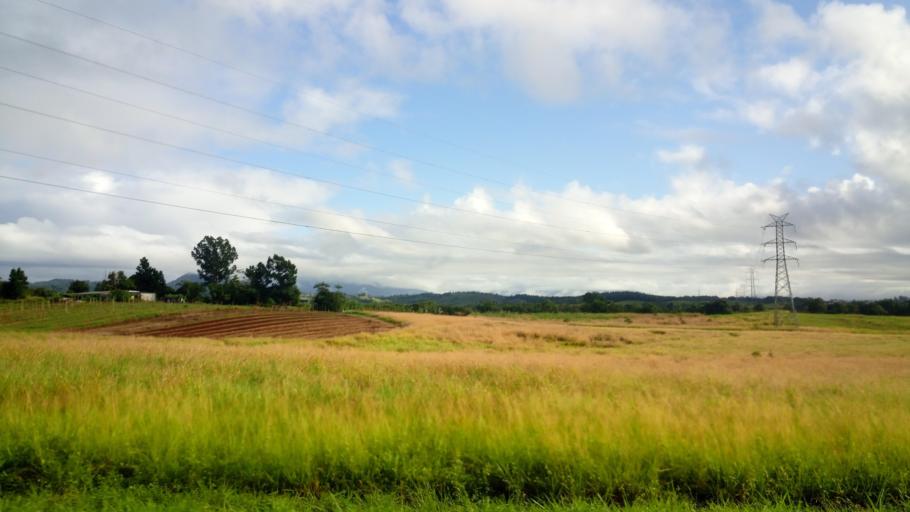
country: AU
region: Queensland
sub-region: Cassowary Coast
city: Innisfail
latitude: -17.5333
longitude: 145.9750
